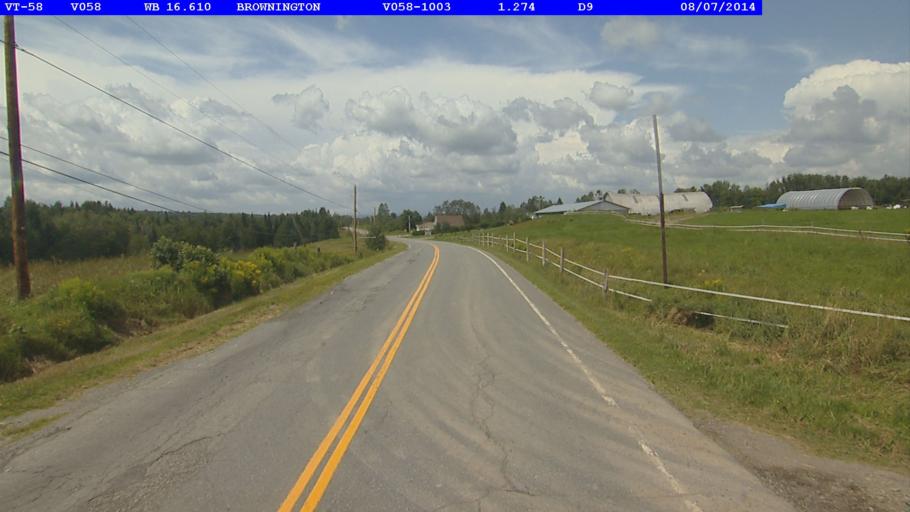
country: US
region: Vermont
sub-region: Orleans County
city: Newport
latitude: 44.8001
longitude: -72.1212
